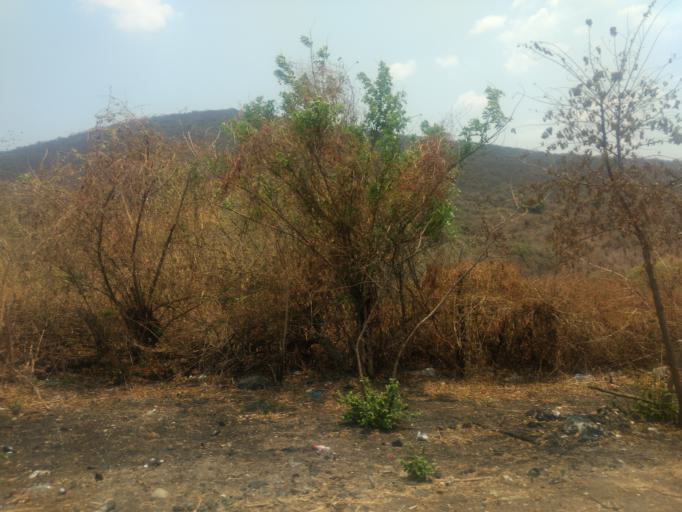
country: MX
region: Morelos
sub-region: Mazatepec
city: Cuauchichinola
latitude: 18.6517
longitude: -99.4018
